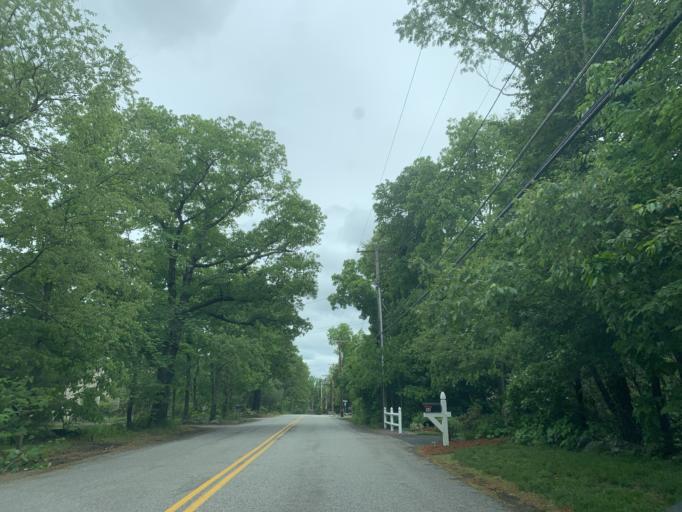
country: US
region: Massachusetts
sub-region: Worcester County
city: Grafton
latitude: 42.1894
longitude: -71.7014
